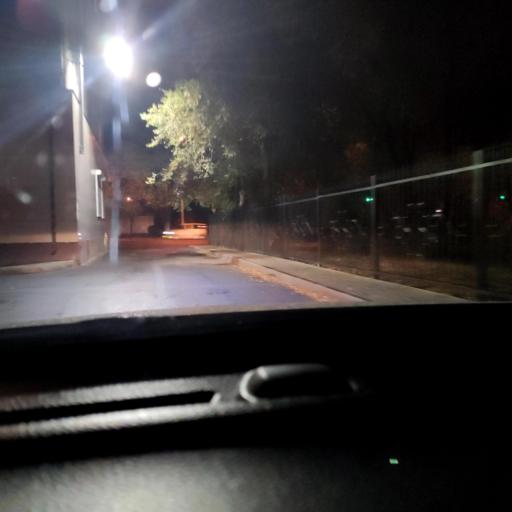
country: RU
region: Voronezj
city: Maslovka
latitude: 51.6131
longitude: 39.2458
